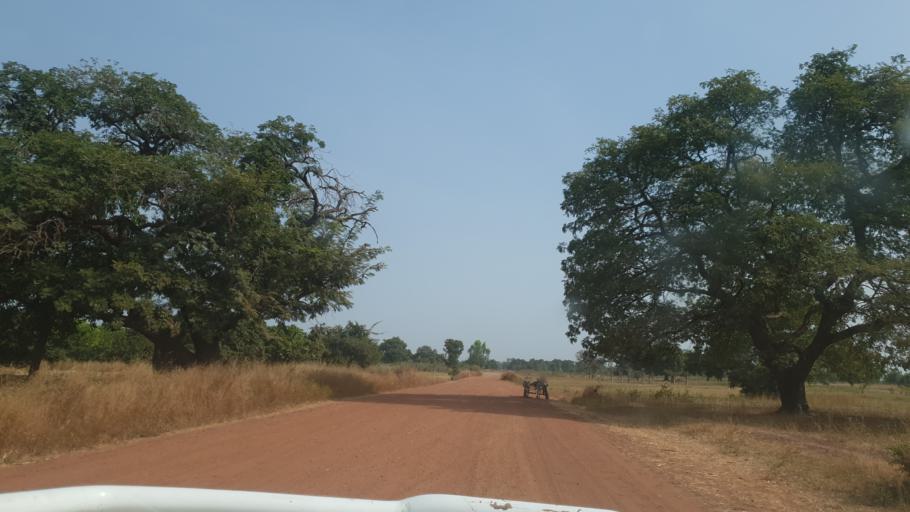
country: ML
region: Koulikoro
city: Dioila
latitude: 12.2256
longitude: -6.2150
